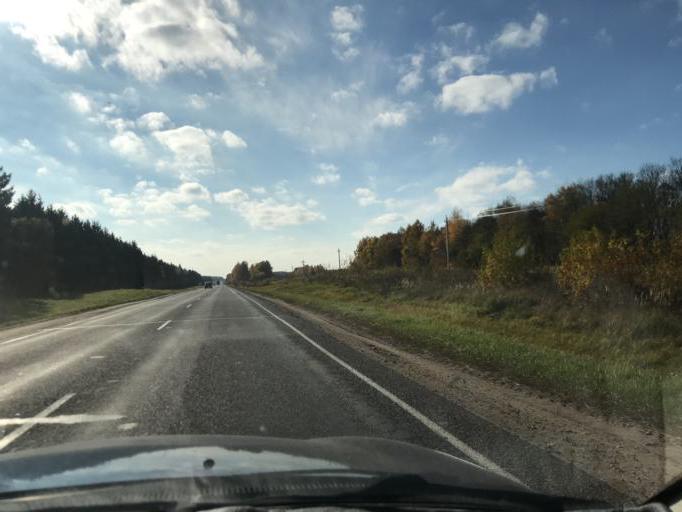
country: BY
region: Grodnenskaya
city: Voranava
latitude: 54.2122
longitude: 25.3520
